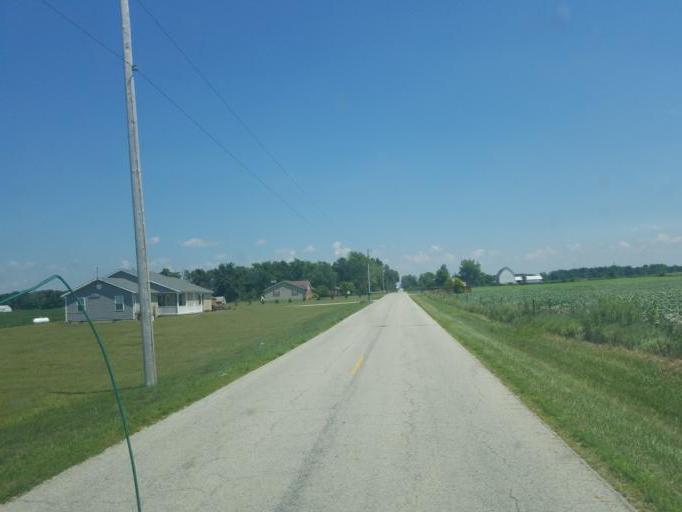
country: US
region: Ohio
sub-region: Shelby County
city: Botkins
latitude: 40.4823
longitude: -84.2008
